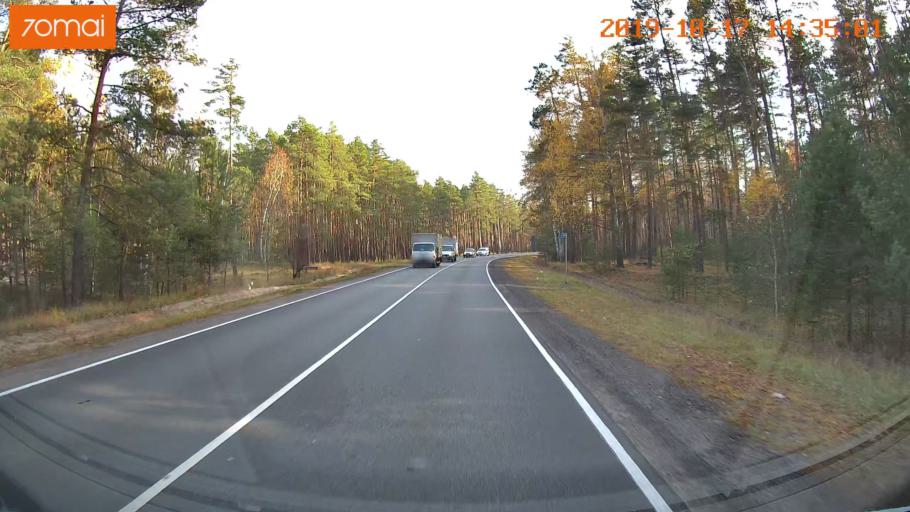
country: RU
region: Rjazan
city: Solotcha
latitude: 54.9048
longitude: 40.0020
